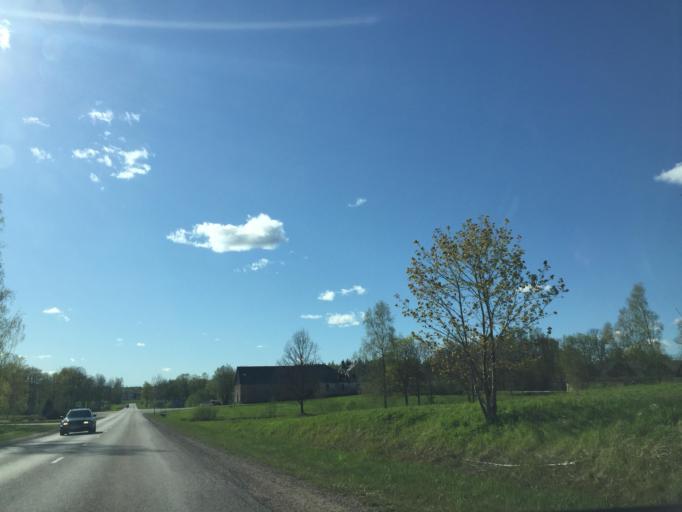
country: LV
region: Madonas Rajons
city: Madona
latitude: 56.8062
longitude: 26.0348
